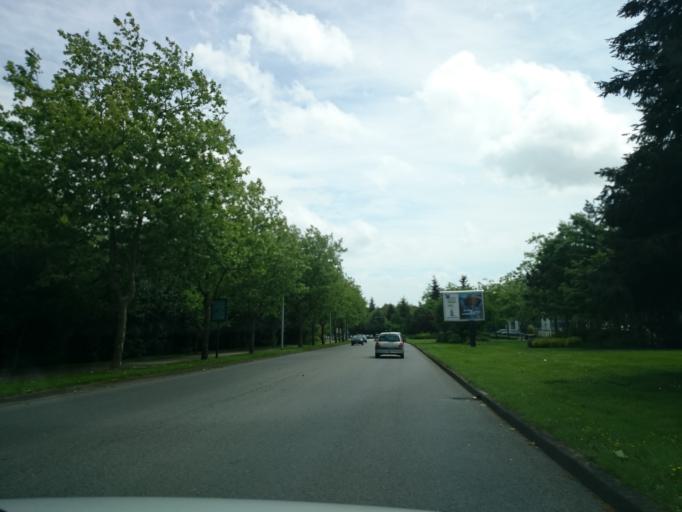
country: FR
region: Brittany
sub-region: Departement du Morbihan
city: Vannes
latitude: 47.6495
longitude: -2.7827
